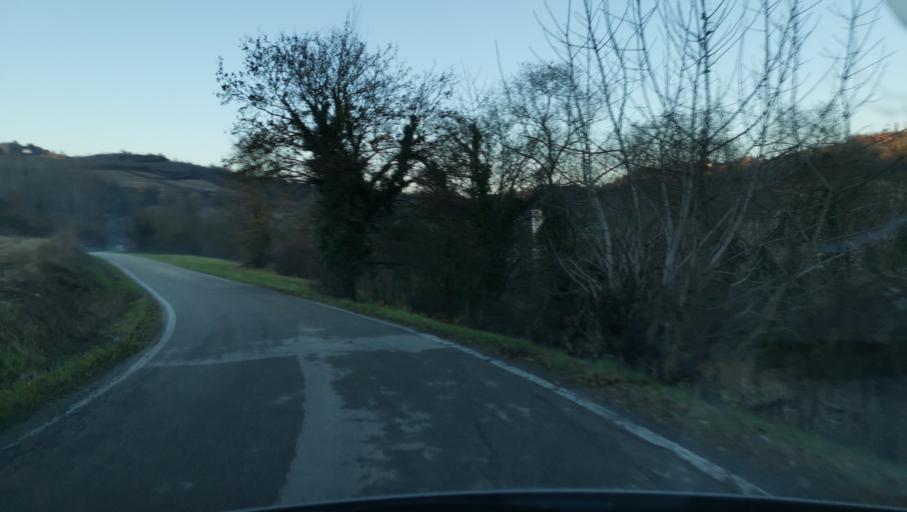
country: IT
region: Piedmont
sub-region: Provincia di Asti
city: Moncucco Torinese
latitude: 45.0667
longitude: 7.9429
